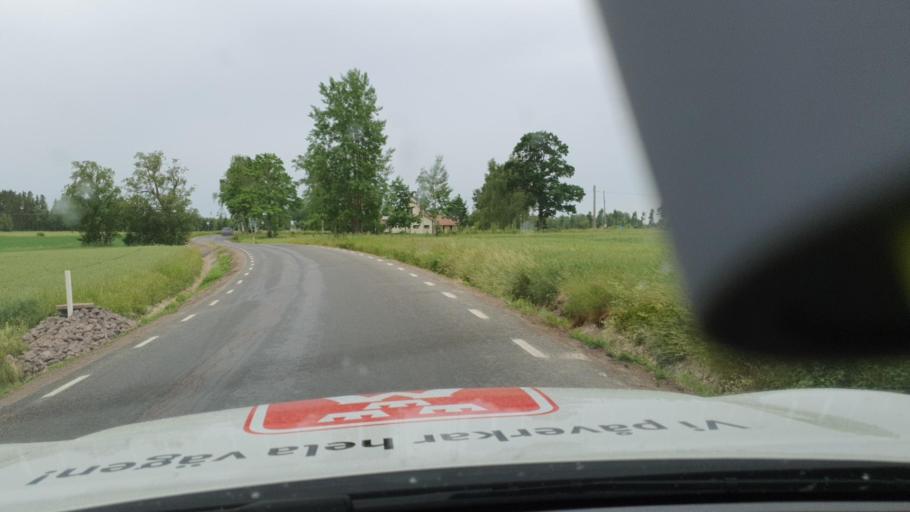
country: SE
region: Vaestra Goetaland
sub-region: Tidaholms Kommun
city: Olofstorp
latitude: 58.3235
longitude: 14.0607
